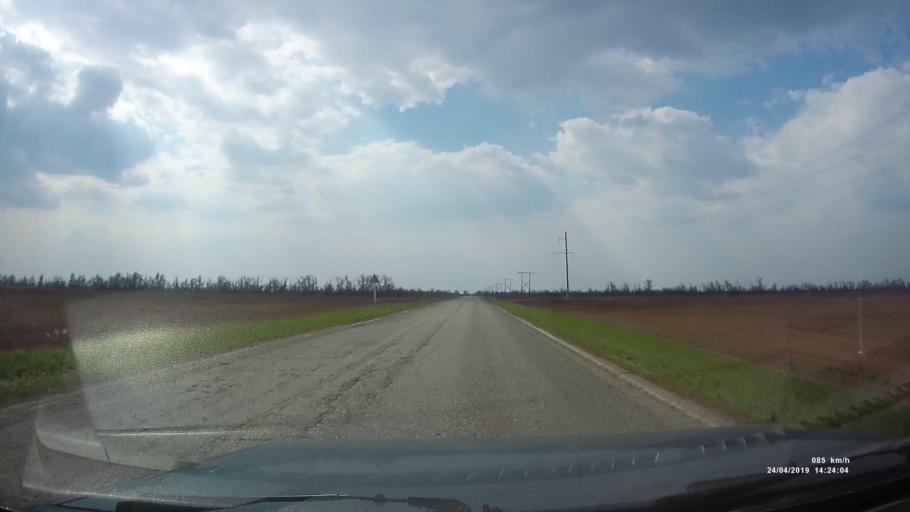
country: RU
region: Kalmykiya
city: Arshan'
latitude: 46.3266
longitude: 44.1047
